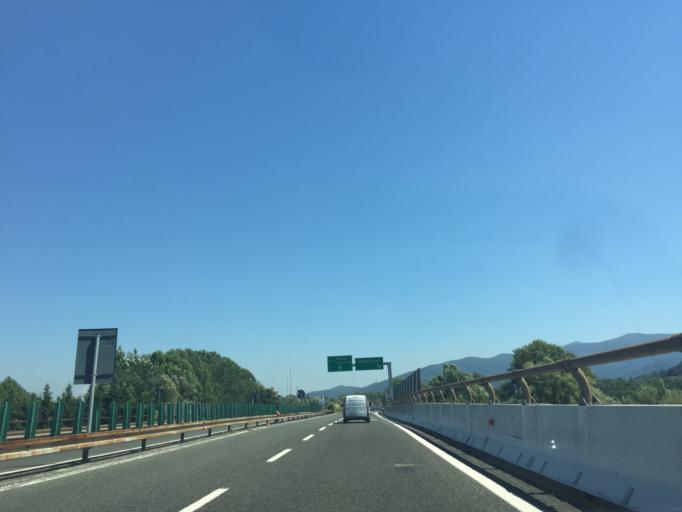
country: IT
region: Tuscany
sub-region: Provincia di Lucca
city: Lucca
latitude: 43.8391
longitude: 10.4626
